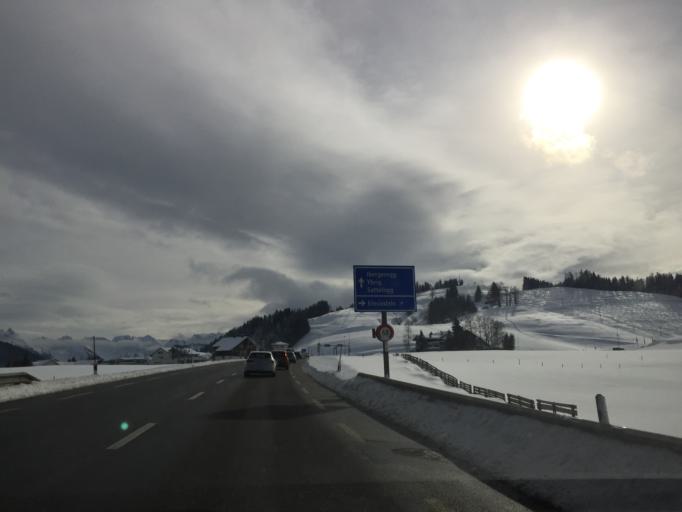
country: CH
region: Schwyz
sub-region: Bezirk Einsiedeln
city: Einsiedeln
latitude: 47.1337
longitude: 8.7638
